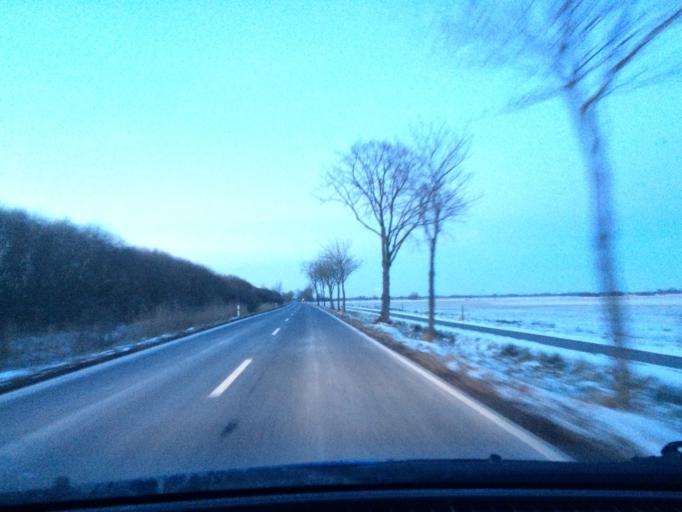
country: DE
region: Lower Saxony
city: Marschacht
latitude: 53.4040
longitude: 10.3562
